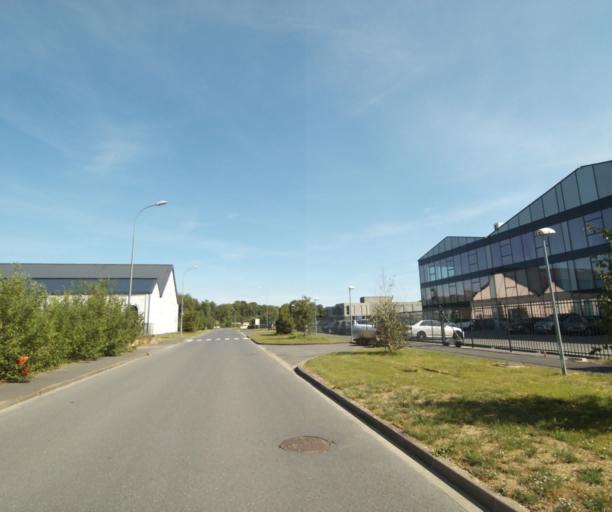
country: FR
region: Champagne-Ardenne
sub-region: Departement des Ardennes
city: Villers-Semeuse
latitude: 49.7424
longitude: 4.7309
